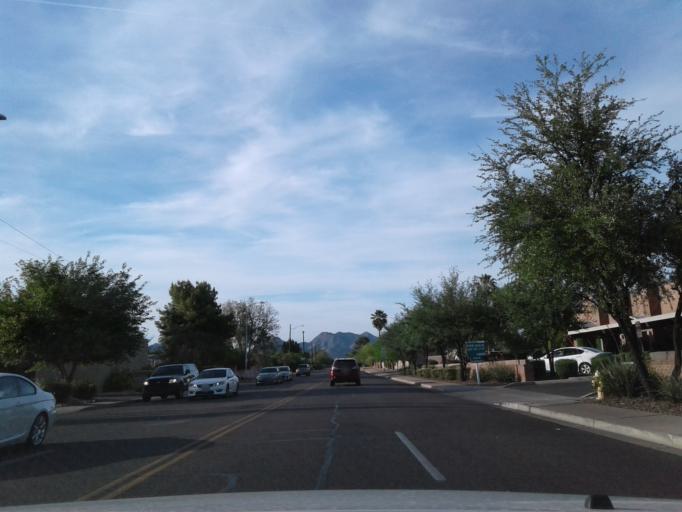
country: US
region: Arizona
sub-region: Maricopa County
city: Paradise Valley
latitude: 33.4955
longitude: -111.9954
